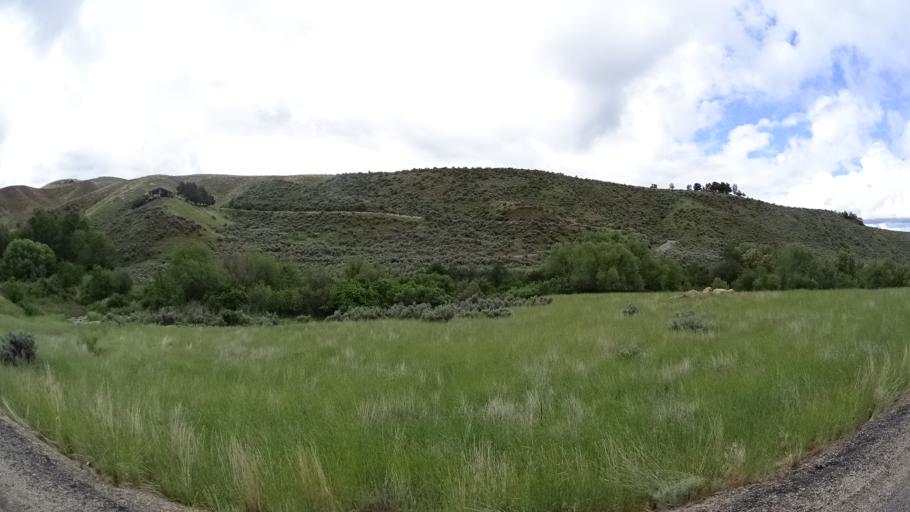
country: US
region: Idaho
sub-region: Ada County
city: Garden City
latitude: 43.6843
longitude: -116.2538
